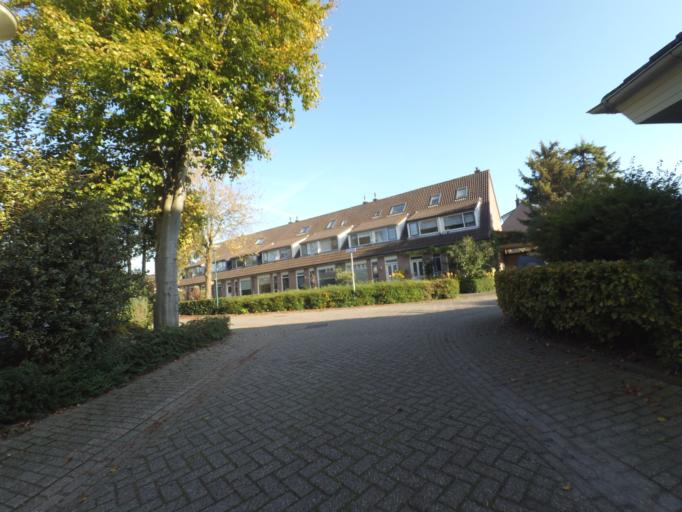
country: NL
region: Utrecht
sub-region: Gemeente Leusden
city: Leusden
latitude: 52.1263
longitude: 5.4385
